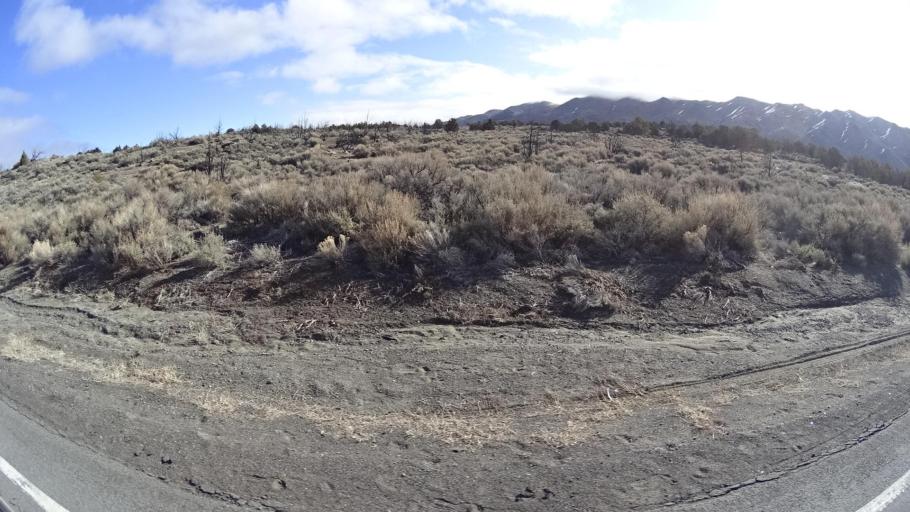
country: US
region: Nevada
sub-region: Washoe County
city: Cold Springs
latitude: 39.7758
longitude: -119.8933
